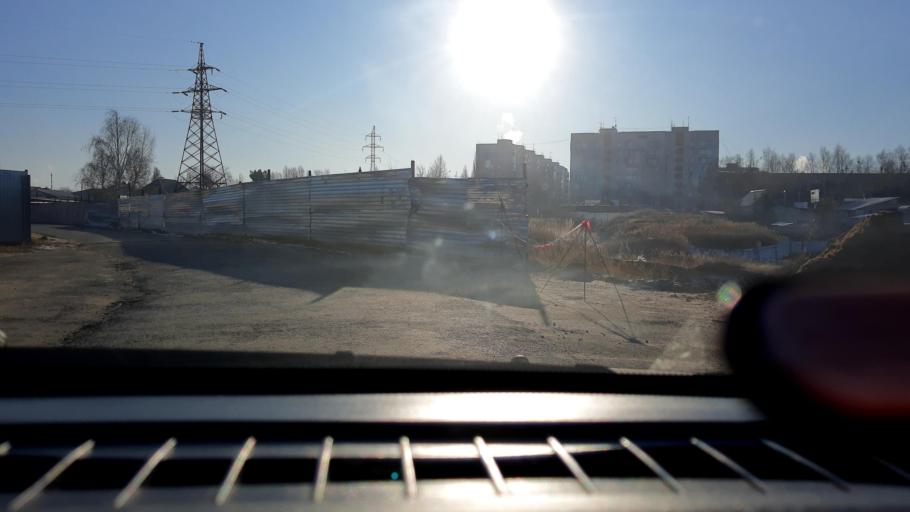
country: RU
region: Nizjnij Novgorod
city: Gorbatovka
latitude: 56.3836
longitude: 43.7988
